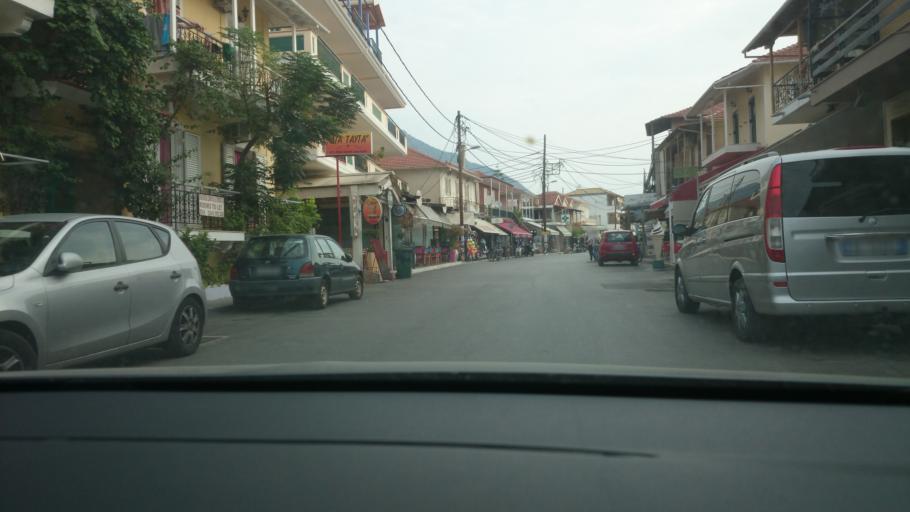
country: GR
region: Ionian Islands
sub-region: Lefkada
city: Nidri
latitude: 38.7064
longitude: 20.7093
